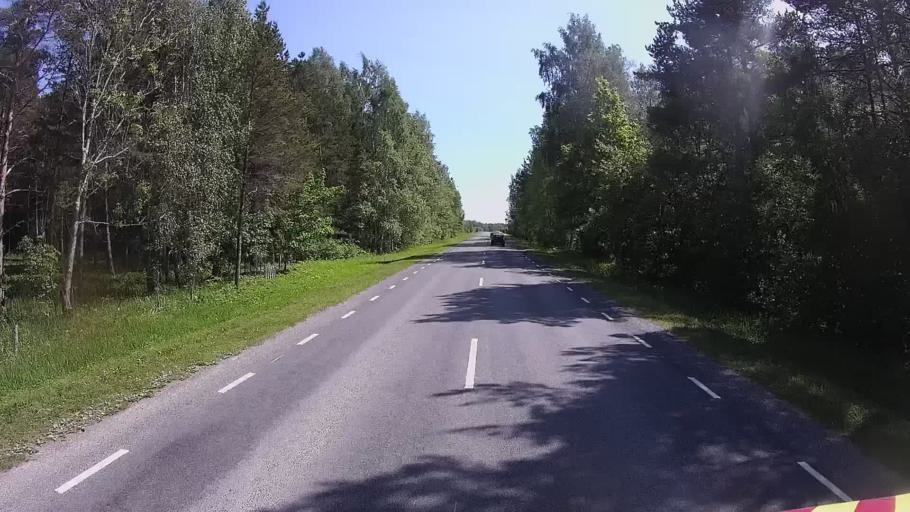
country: EE
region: Saare
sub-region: Kuressaare linn
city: Kuressaare
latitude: 58.2813
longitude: 22.4625
